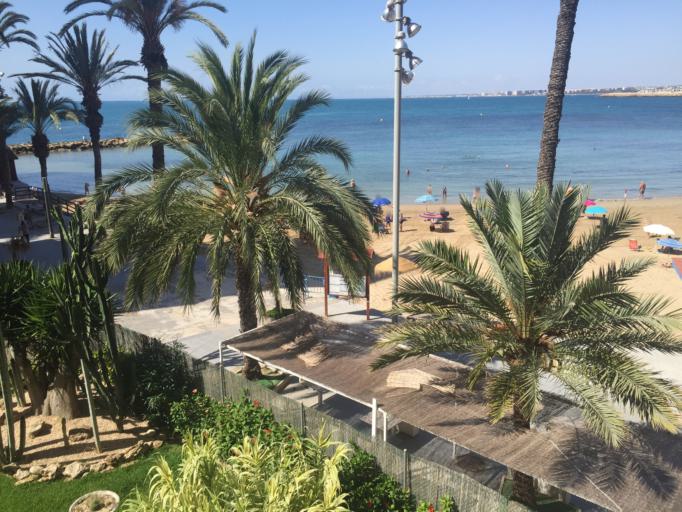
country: ES
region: Valencia
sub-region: Provincia de Alicante
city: Torrevieja
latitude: 37.9770
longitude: -0.6676
